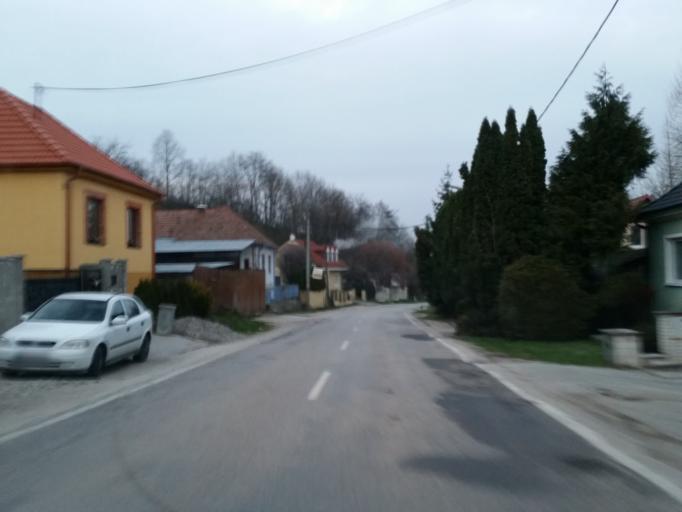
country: SK
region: Trnavsky
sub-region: Okres Trnava
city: Piestany
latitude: 48.5783
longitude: 17.8522
